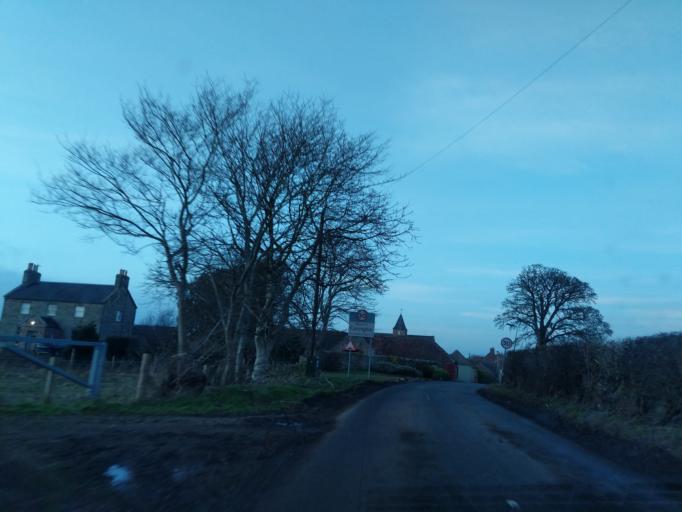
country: GB
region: Scotland
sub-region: Midlothian
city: Bonnyrigg
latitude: 55.8324
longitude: -3.0882
